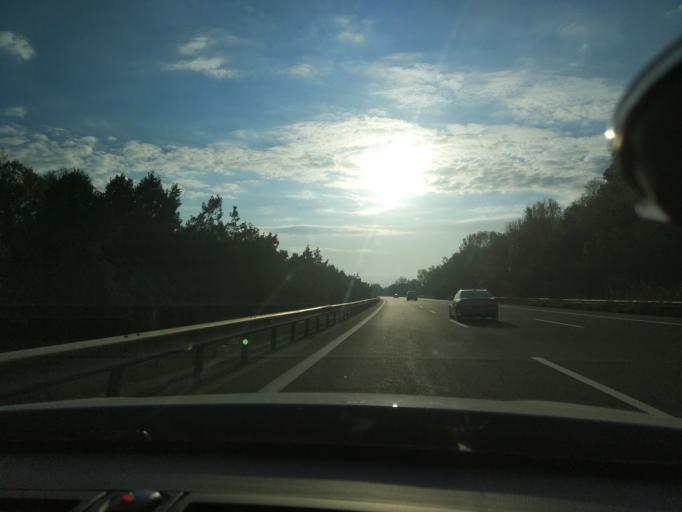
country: TR
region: Duzce
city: Duzce
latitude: 40.8059
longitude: 31.1534
